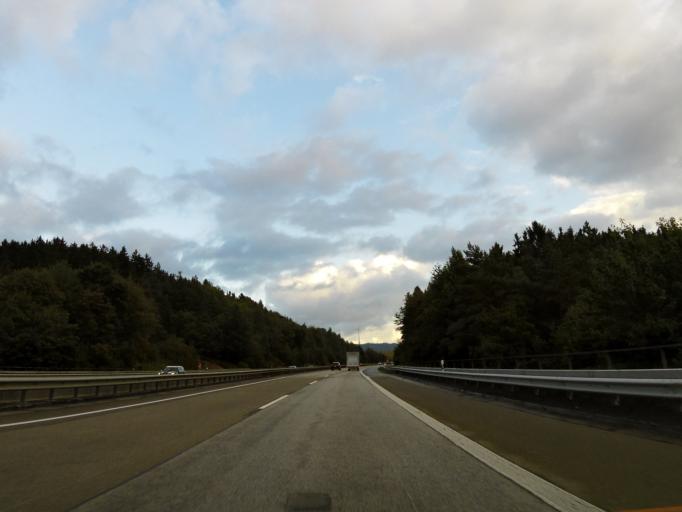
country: DE
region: Rheinland-Pfalz
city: Rheinbollen
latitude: 50.0225
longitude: 7.6768
